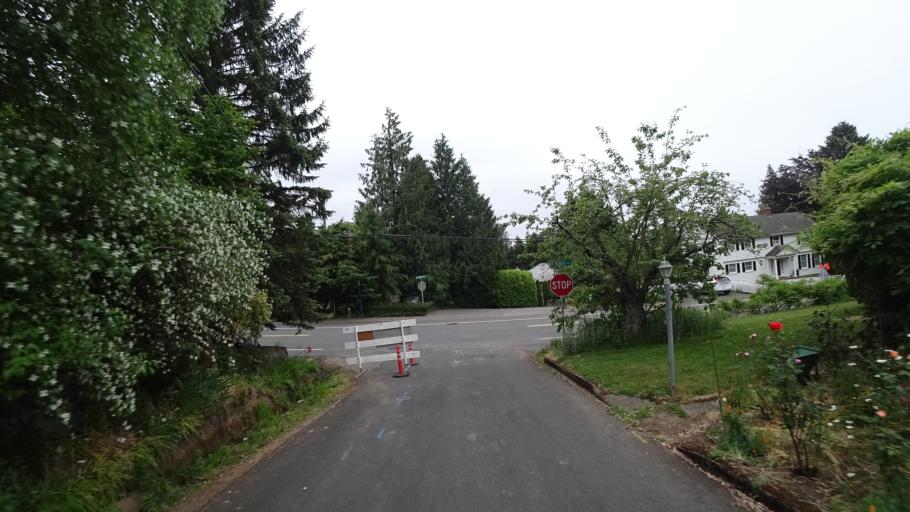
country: US
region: Oregon
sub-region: Multnomah County
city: Portland
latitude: 45.4889
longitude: -122.7065
